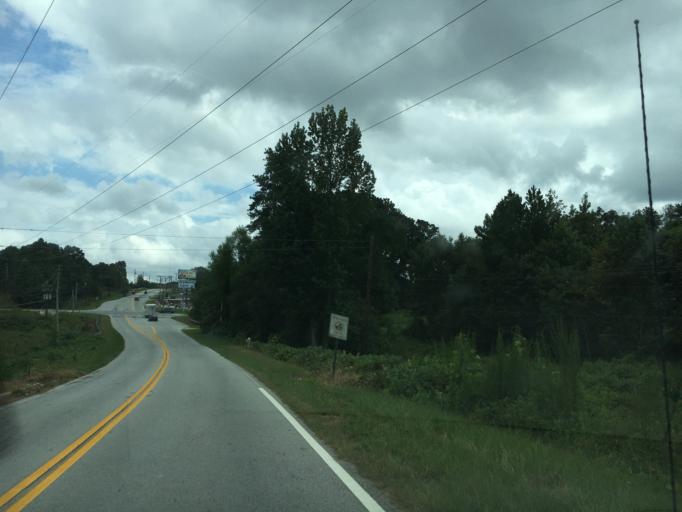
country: US
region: Georgia
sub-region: Rockdale County
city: Lakeview Estates
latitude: 33.6882
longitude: -84.0337
